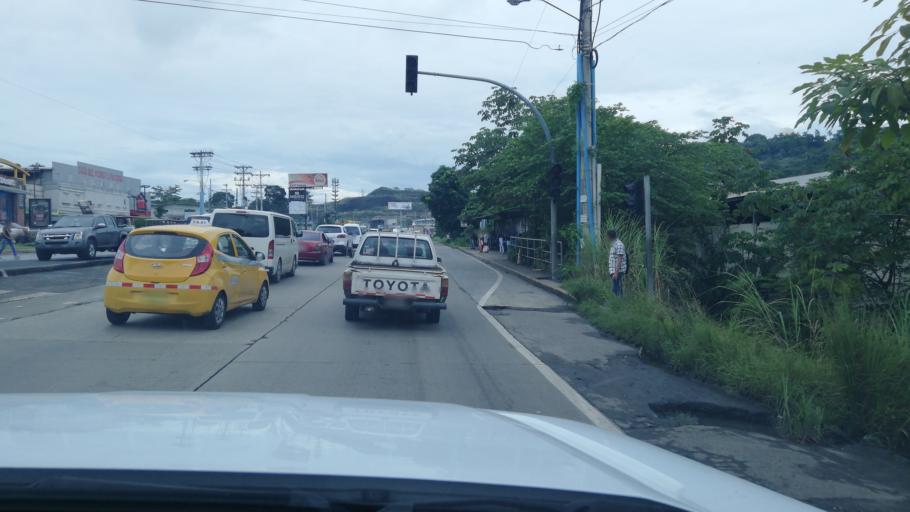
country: PA
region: Panama
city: Las Cumbres
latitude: 9.0691
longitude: -79.5190
